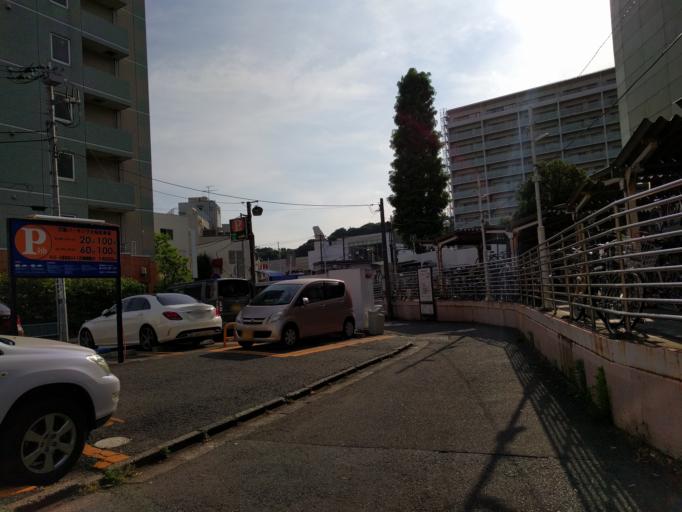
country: JP
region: Kanagawa
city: Kamakura
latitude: 35.3548
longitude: 139.5334
